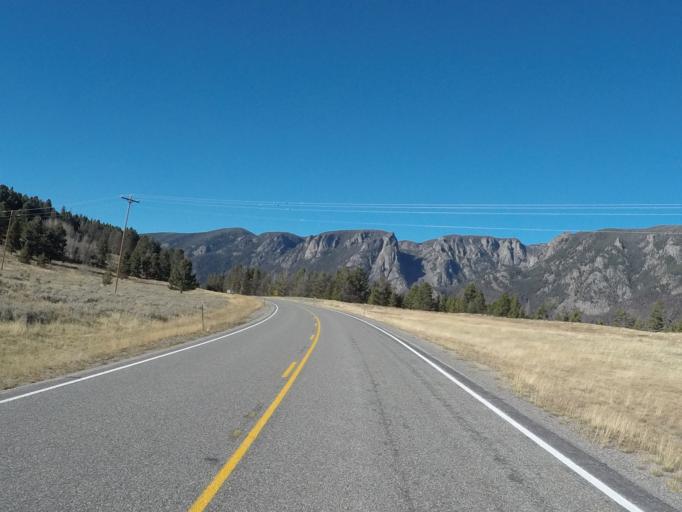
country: US
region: Montana
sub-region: Carbon County
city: Red Lodge
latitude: 44.8421
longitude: -109.4984
